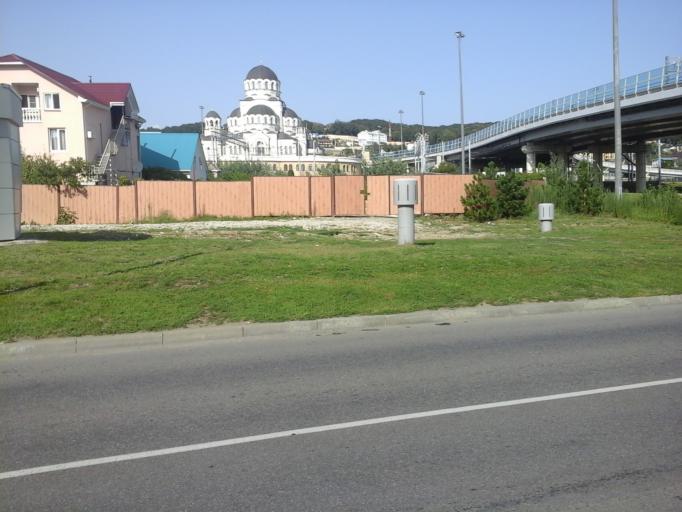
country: RU
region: Krasnodarskiy
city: Adler
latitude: 43.4134
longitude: 39.9677
